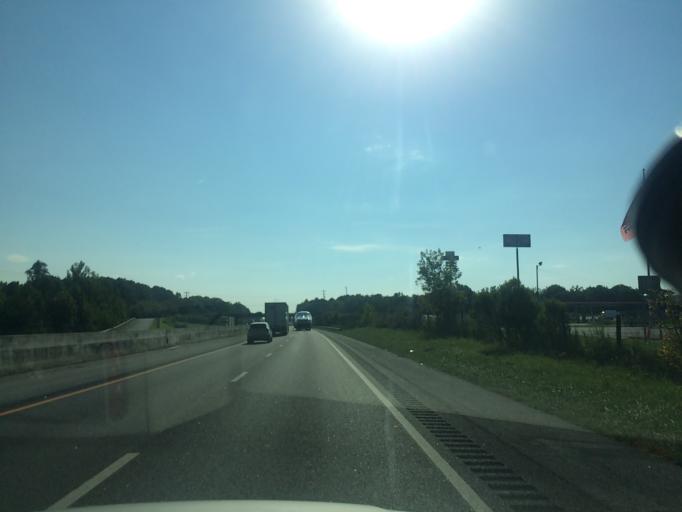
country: US
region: South Carolina
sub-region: Cherokee County
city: Blacksburg
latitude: 35.1299
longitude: -81.5481
